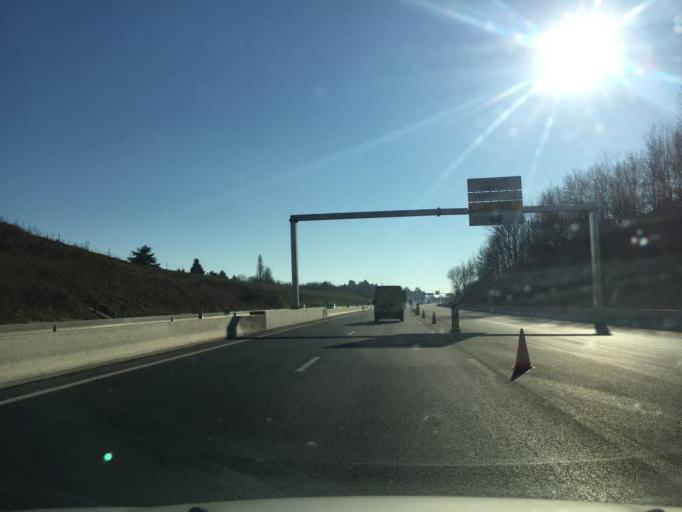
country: FR
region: Rhone-Alpes
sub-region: Departement du Rhone
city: Limonest
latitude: 45.8326
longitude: 4.7598
